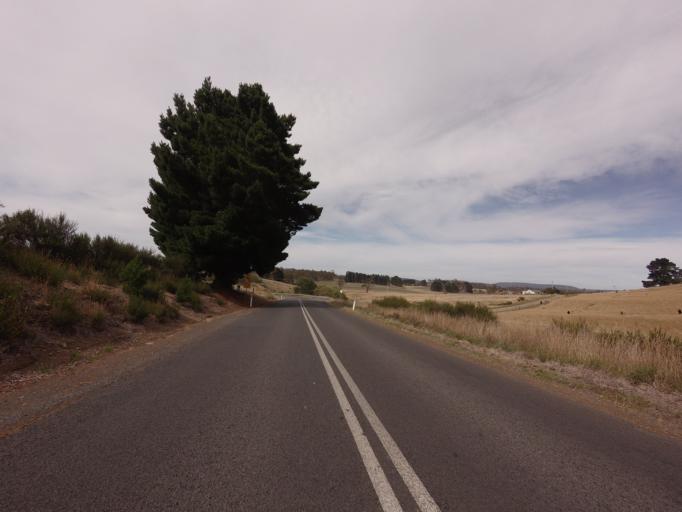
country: AU
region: Tasmania
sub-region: Sorell
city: Sorell
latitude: -42.4289
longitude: 147.4660
